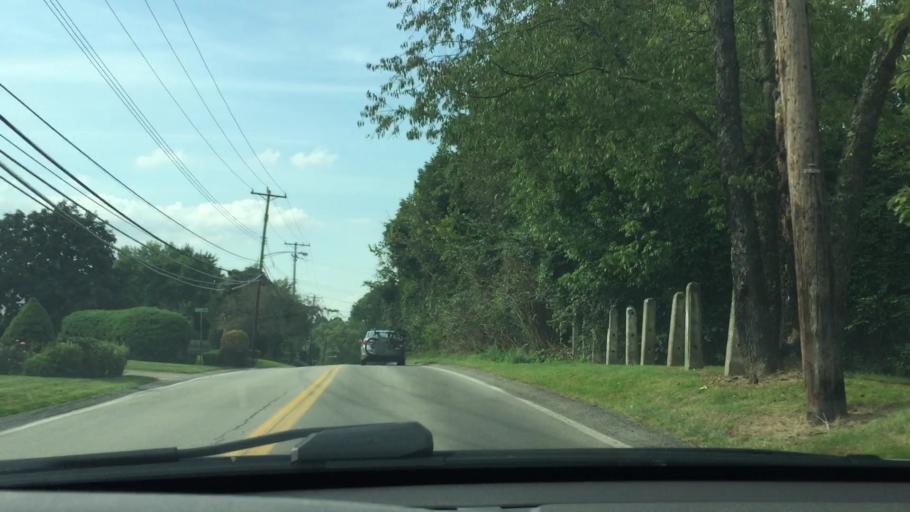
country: US
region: Pennsylvania
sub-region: Westmoreland County
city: Level Green
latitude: 40.4165
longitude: -79.7407
